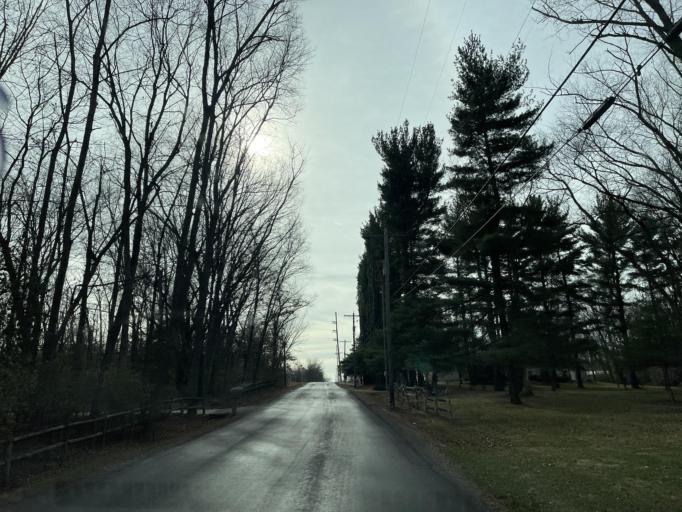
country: US
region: Illinois
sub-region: Sangamon County
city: Leland Grove
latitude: 39.7850
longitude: -89.7339
